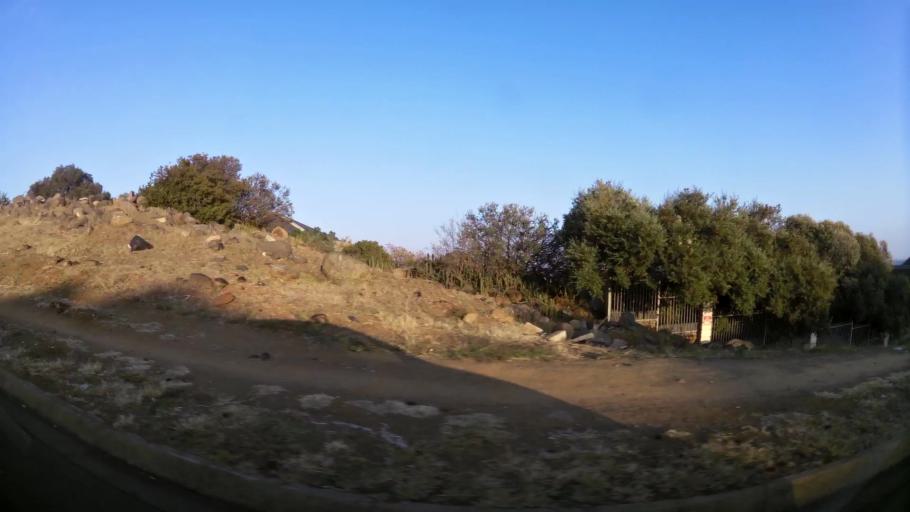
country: ZA
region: Orange Free State
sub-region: Mangaung Metropolitan Municipality
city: Bloemfontein
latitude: -29.0896
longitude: 26.1642
